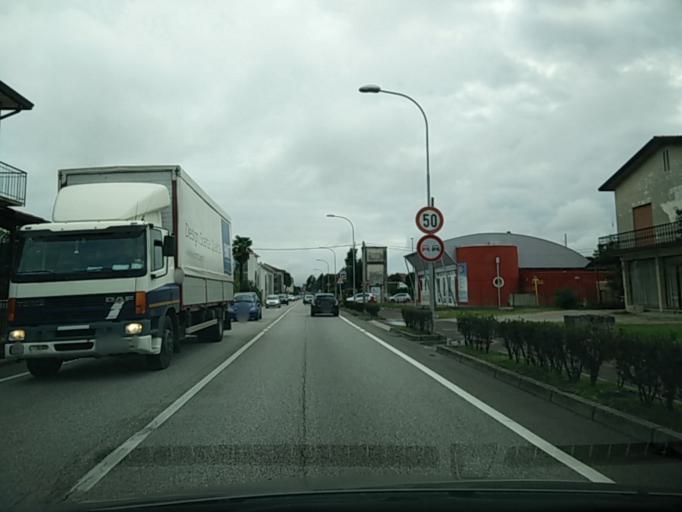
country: IT
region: Veneto
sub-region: Provincia di Padova
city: Cittadella
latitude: 45.6636
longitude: 11.7798
